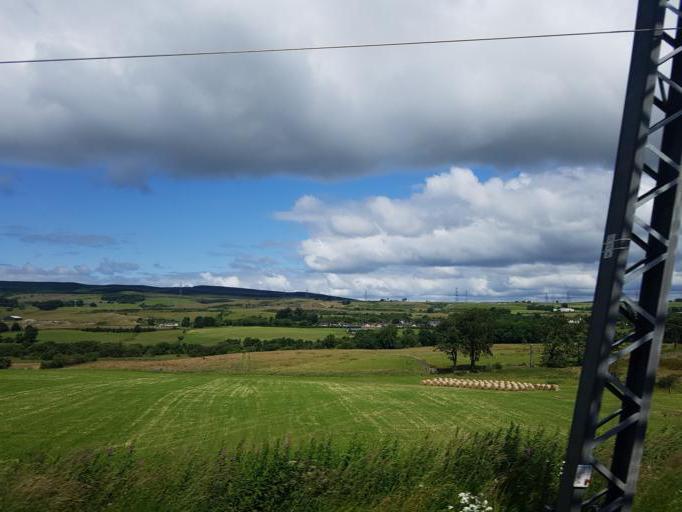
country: GB
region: Scotland
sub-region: North Lanarkshire
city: Cumbernauld
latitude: 55.9814
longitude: -3.9675
